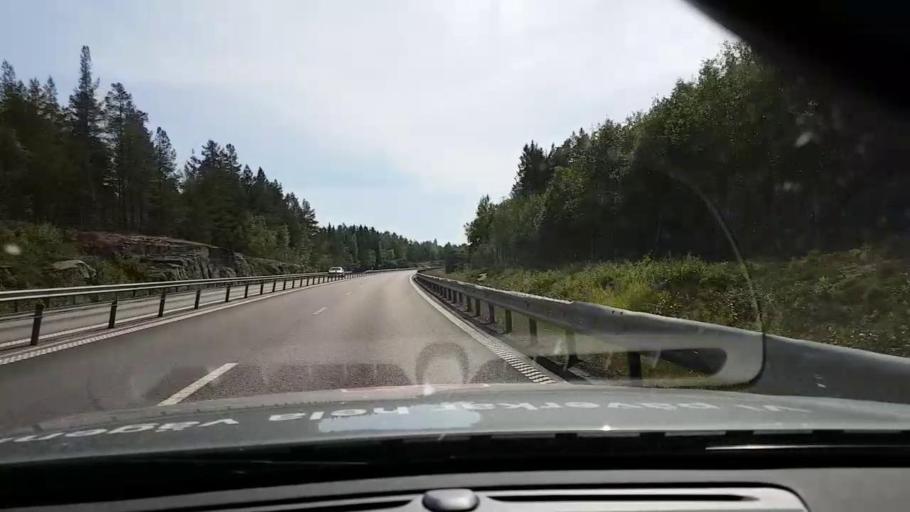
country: SE
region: Vaesternorrland
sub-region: OErnskoeldsviks Kommun
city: Husum
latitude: 63.3887
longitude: 19.1944
